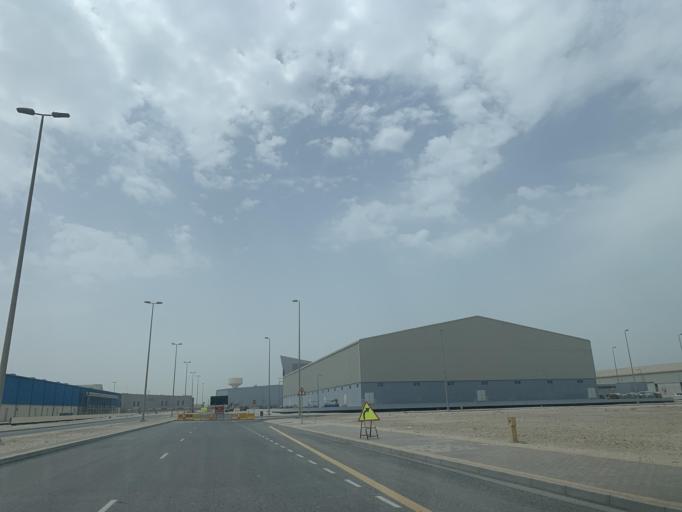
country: BH
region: Muharraq
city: Al Hadd
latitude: 26.2212
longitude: 50.6909
